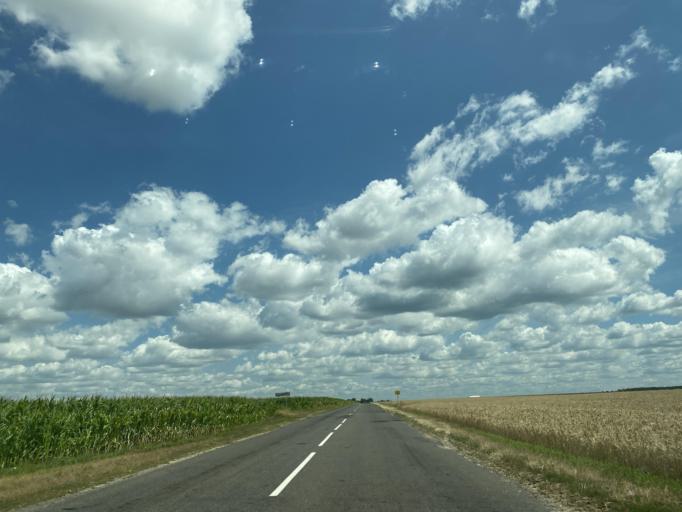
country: BY
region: Brest
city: Ivanava
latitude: 52.1728
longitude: 25.5640
